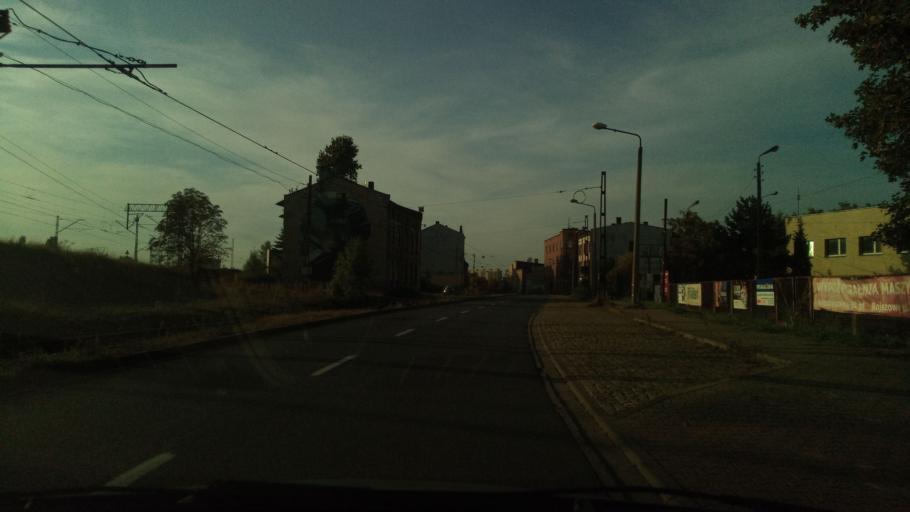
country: PL
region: Silesian Voivodeship
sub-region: Sosnowiec
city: Sosnowiec
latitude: 50.2583
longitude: 19.1133
